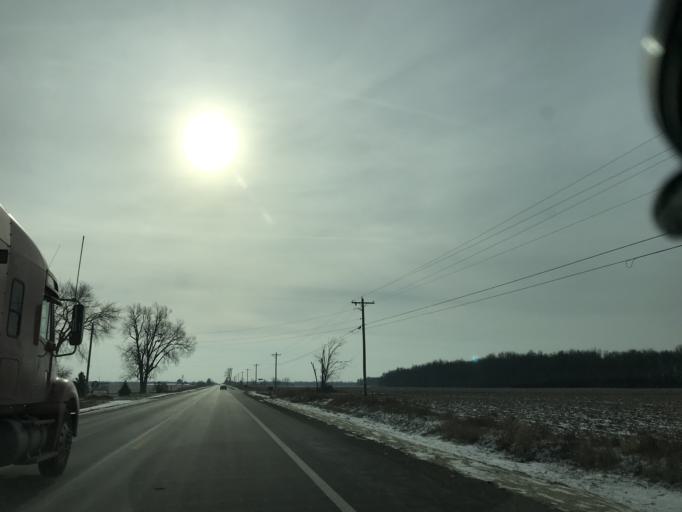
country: US
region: Michigan
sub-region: Ionia County
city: Lake Odessa
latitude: 42.8372
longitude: -85.0746
